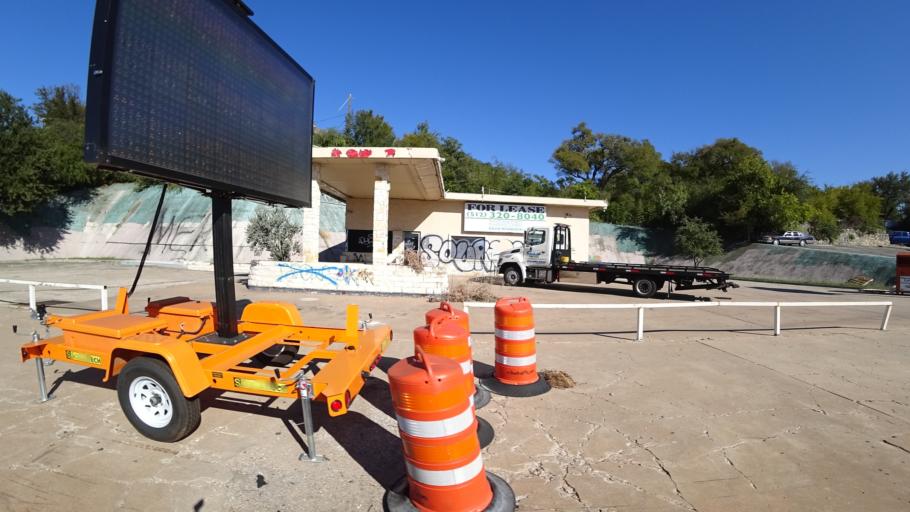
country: US
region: Texas
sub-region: Travis County
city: Austin
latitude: 30.2453
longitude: -97.7345
